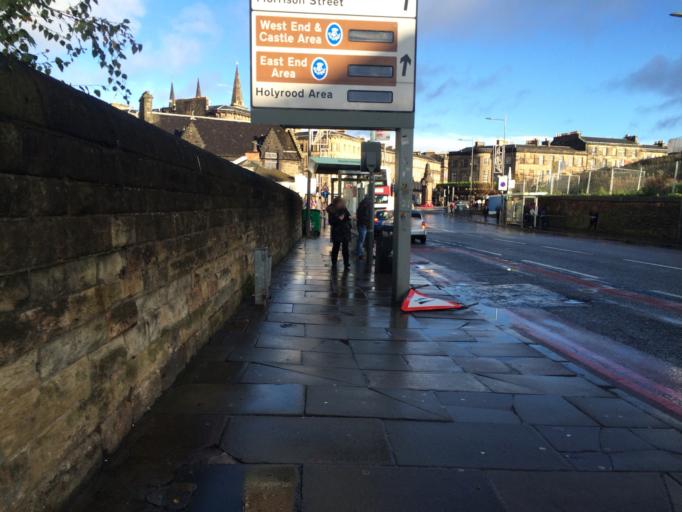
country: GB
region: Scotland
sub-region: Edinburgh
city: Edinburgh
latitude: 55.9456
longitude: -3.2173
